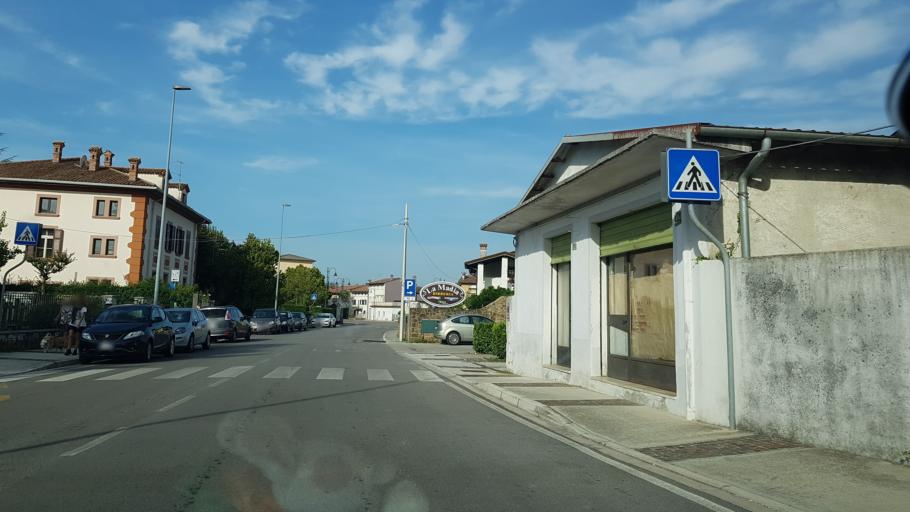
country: IT
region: Friuli Venezia Giulia
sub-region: Provincia di Gorizia
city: Mossa
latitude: 45.9387
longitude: 13.5499
